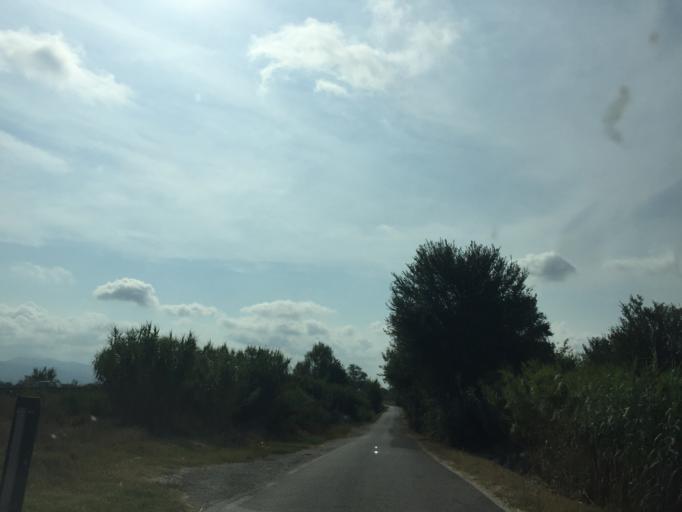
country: IT
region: Tuscany
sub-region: Provincia di Pistoia
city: Cintolese
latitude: 43.8379
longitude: 10.8219
